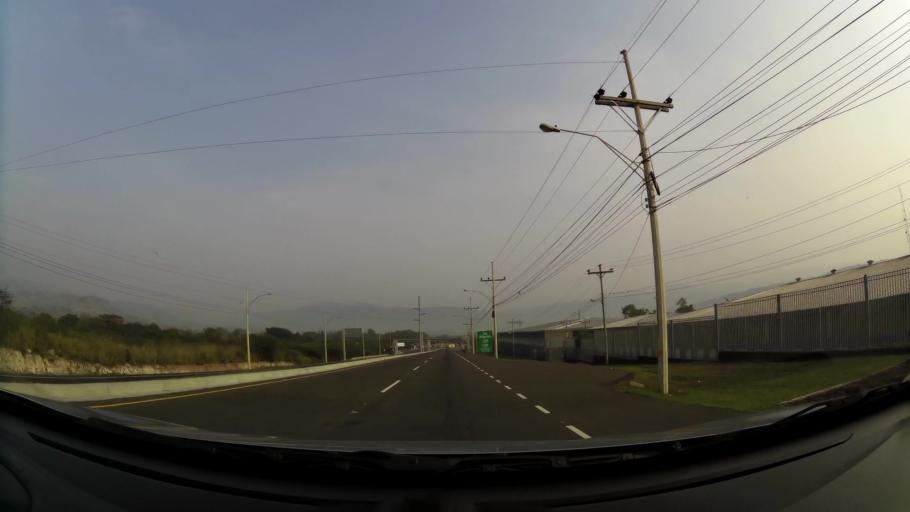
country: HN
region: Francisco Morazan
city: Tamara
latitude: 14.2072
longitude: -87.3504
